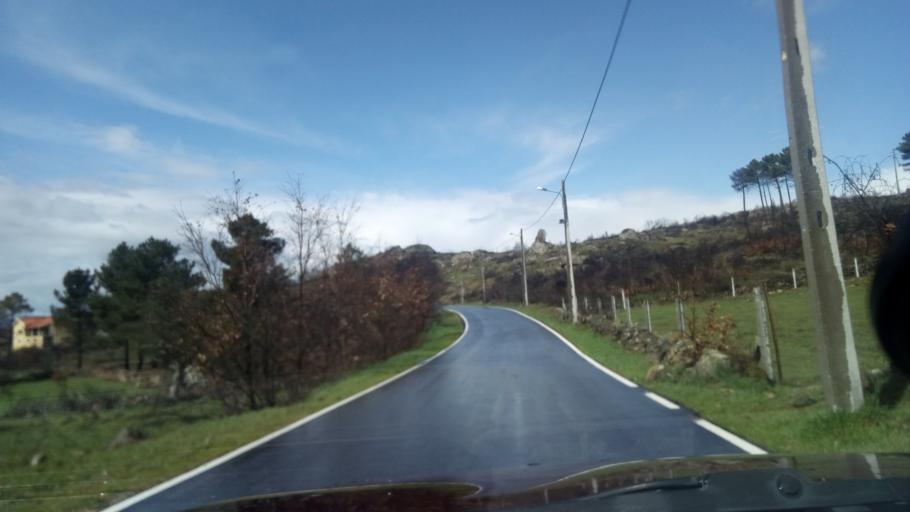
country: PT
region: Guarda
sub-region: Fornos de Algodres
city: Fornos de Algodres
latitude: 40.5846
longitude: -7.4781
